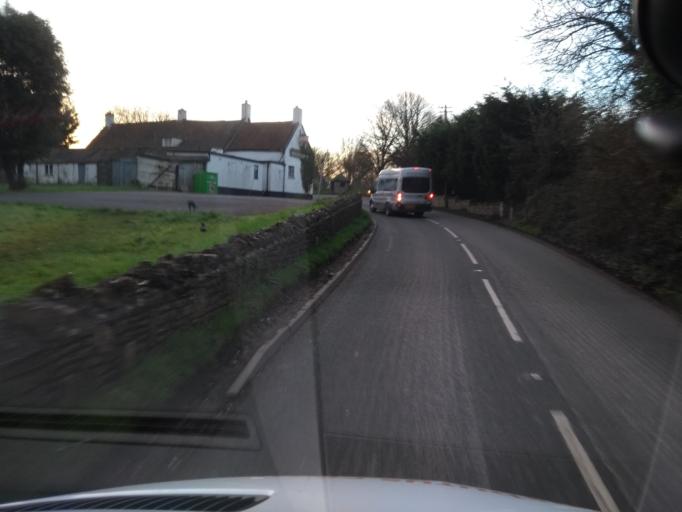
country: GB
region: England
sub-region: Somerset
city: Wedmore
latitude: 51.2256
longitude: -2.8482
